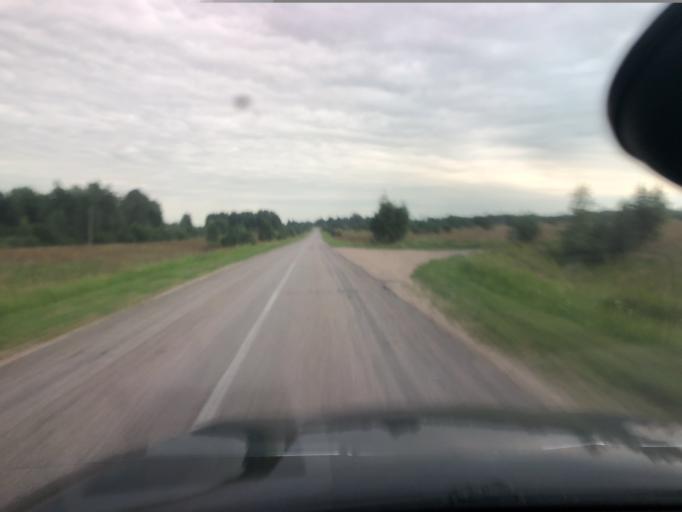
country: RU
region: Jaroslavl
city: Petrovsk
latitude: 57.0020
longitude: 39.0338
